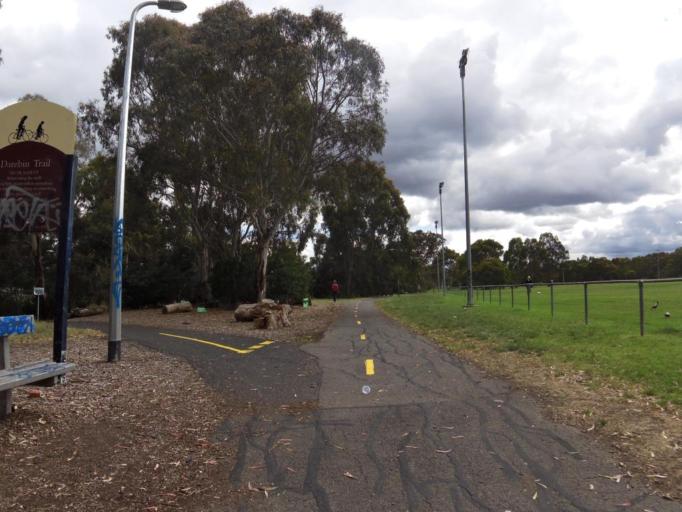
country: AU
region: Victoria
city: Heidelberg West
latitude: -37.7377
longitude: 145.0330
